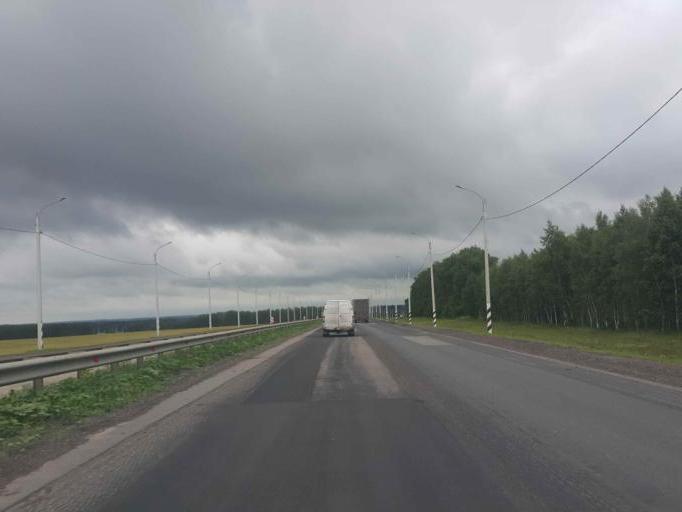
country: RU
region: Tambov
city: Selezni
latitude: 52.7410
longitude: 41.2179
